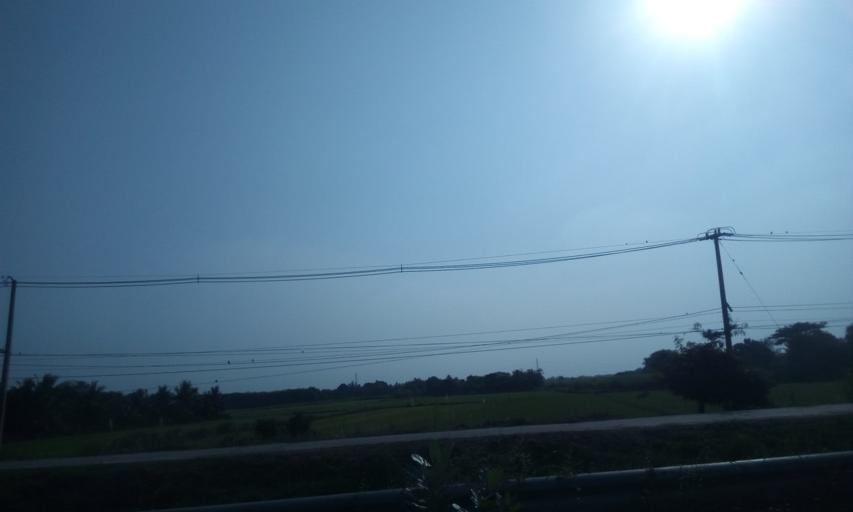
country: TH
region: Sing Buri
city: Sing Buri
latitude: 14.8498
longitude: 100.4156
